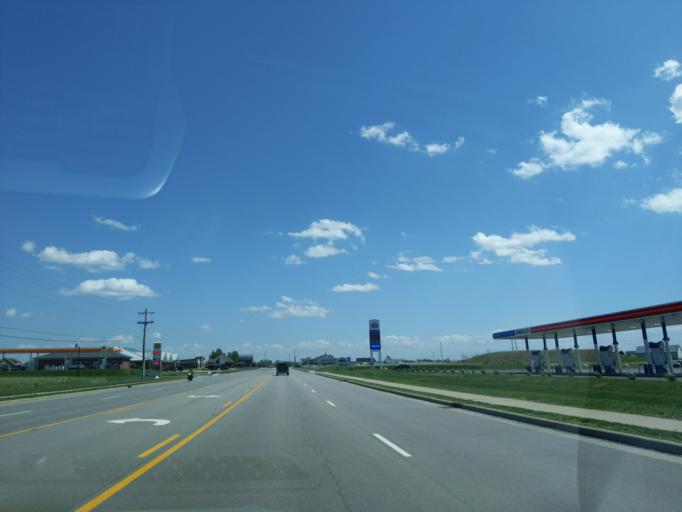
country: US
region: Indiana
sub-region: Decatur County
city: Greensburg
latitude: 39.3549
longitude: -85.5074
